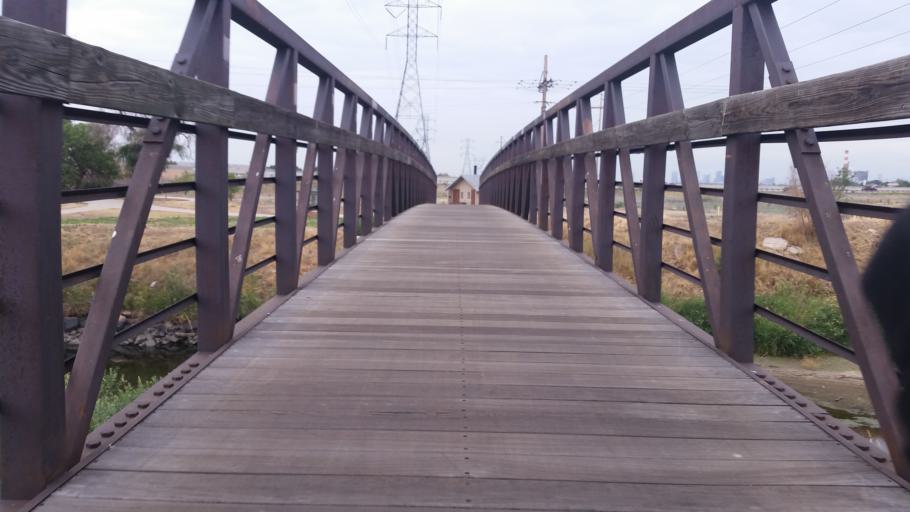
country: US
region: Colorado
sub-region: Adams County
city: Welby
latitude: 39.8278
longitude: -104.9501
